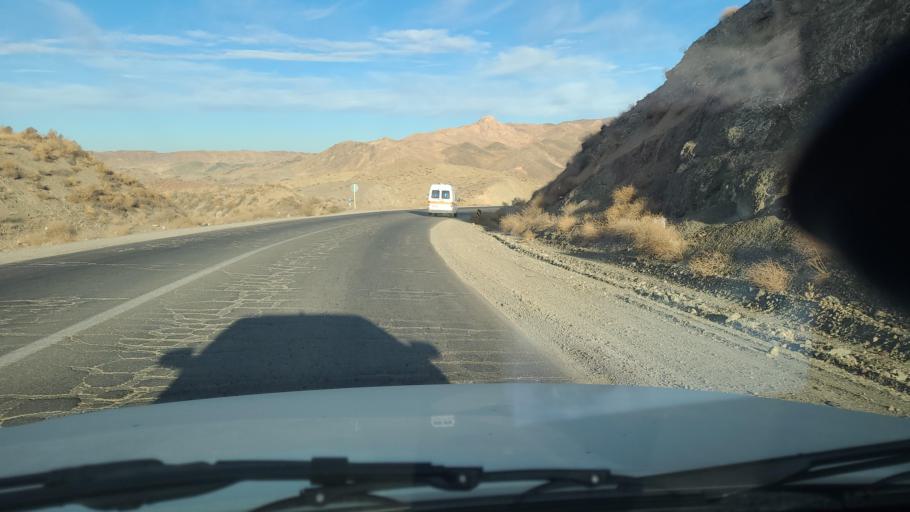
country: IR
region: Razavi Khorasan
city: Sabzevar
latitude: 36.4188
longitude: 57.5561
